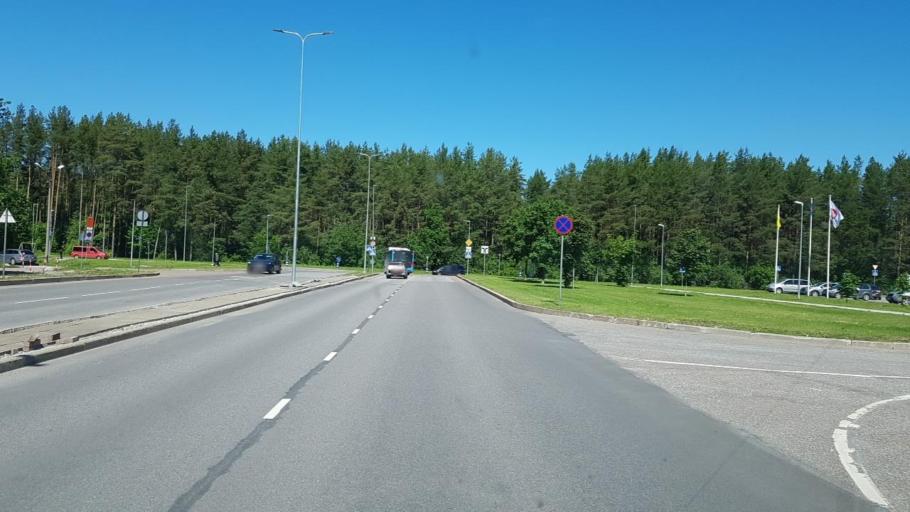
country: EE
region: Ida-Virumaa
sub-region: Narva linn
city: Narva
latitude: 59.3908
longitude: 28.1716
